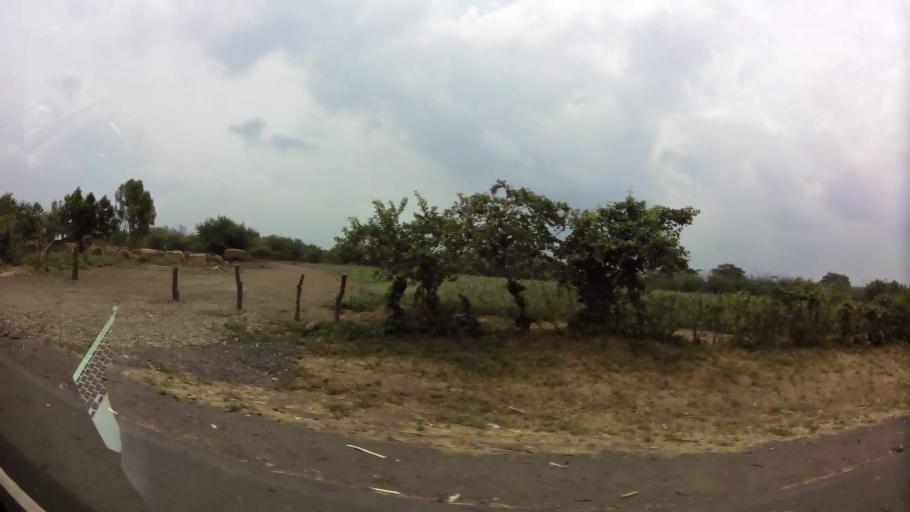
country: NI
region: Chinandega
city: Posoltega
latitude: 12.5500
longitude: -86.9331
